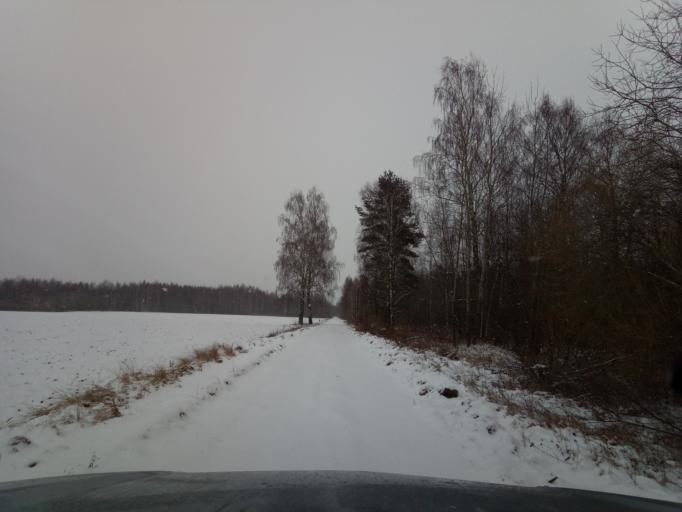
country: LT
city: Ramygala
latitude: 55.5868
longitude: 24.3719
